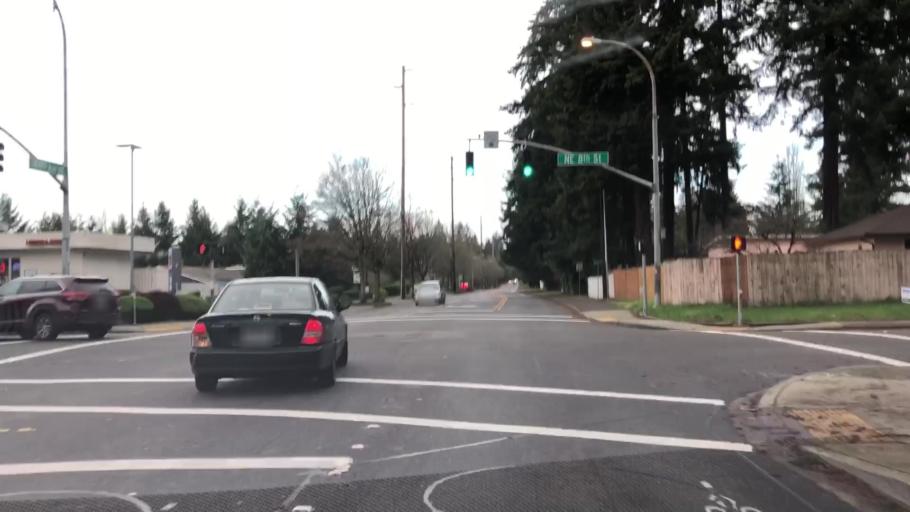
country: US
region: Washington
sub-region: King County
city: West Lake Sammamish
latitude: 47.6167
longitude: -122.1217
